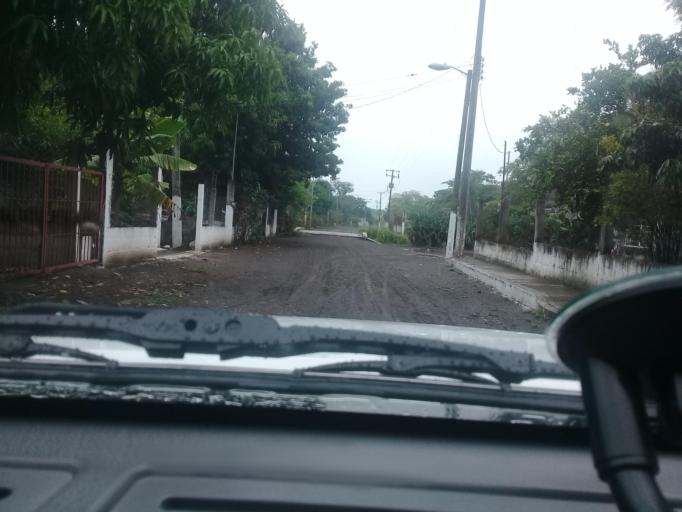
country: MX
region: Veracruz
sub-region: Puente Nacional
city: Cabezas
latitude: 19.3578
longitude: -96.3793
